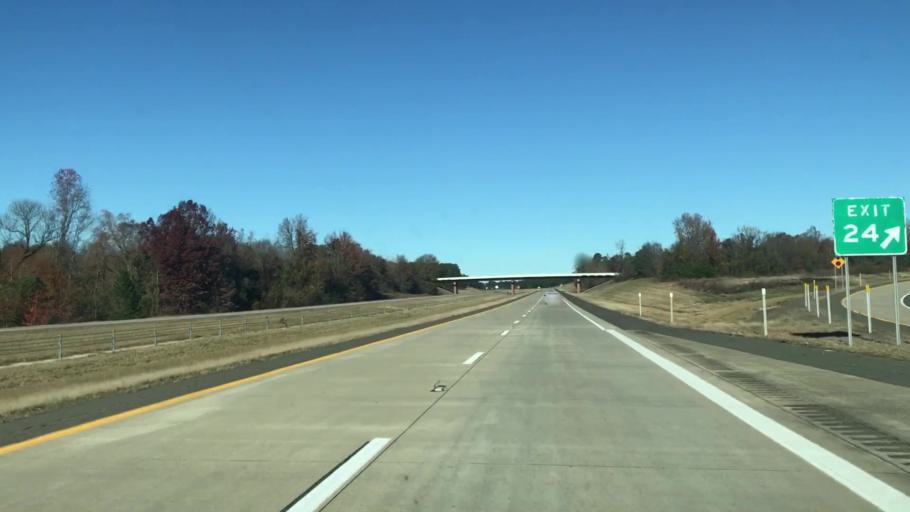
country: US
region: Texas
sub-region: Bowie County
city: Texarkana
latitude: 33.3289
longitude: -93.9573
